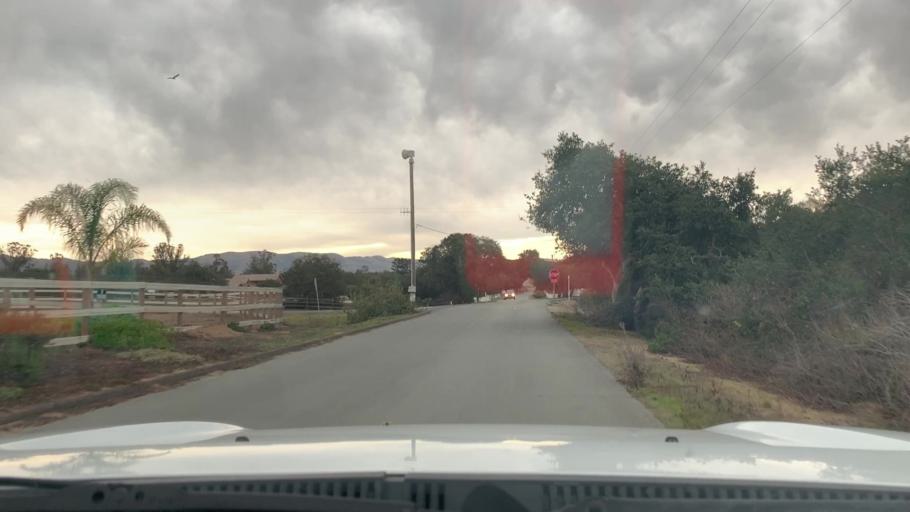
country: US
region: California
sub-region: San Luis Obispo County
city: Callender
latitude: 35.0657
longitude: -120.5568
